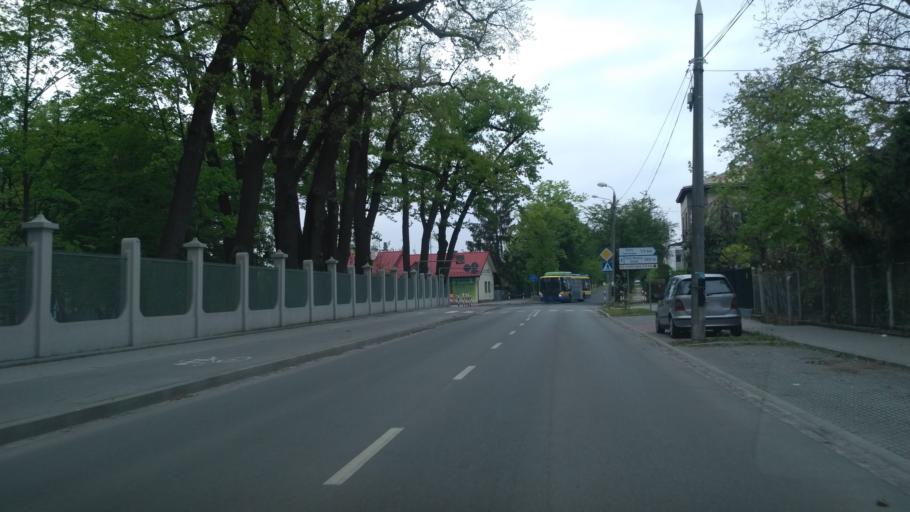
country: PL
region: Lesser Poland Voivodeship
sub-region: Powiat tarnowski
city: Tarnow
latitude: 50.0203
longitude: 20.9872
